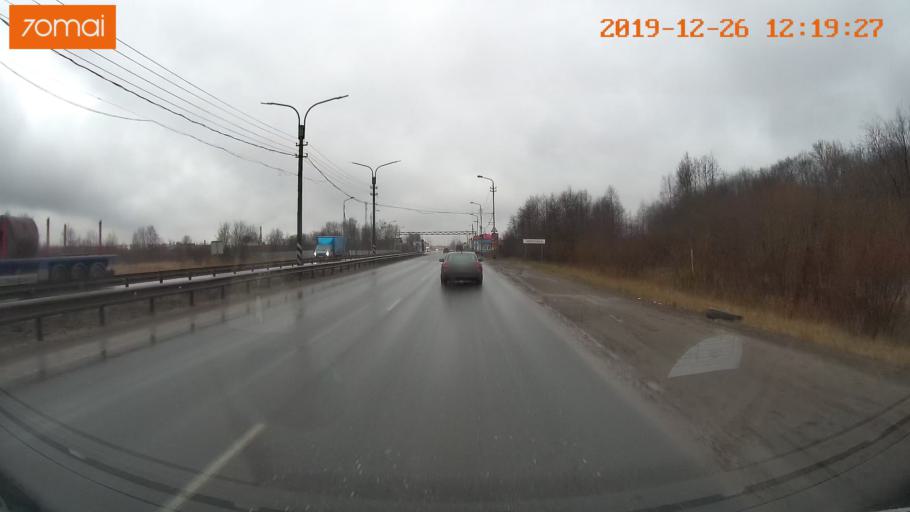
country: RU
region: Vologda
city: Tonshalovo
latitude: 59.1678
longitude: 37.9369
